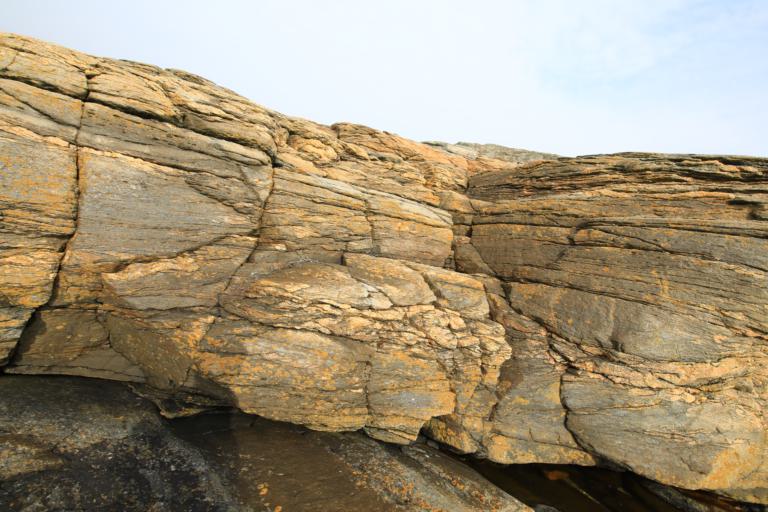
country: SE
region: Halland
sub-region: Kungsbacka Kommun
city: Frillesas
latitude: 57.2489
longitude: 12.0911
